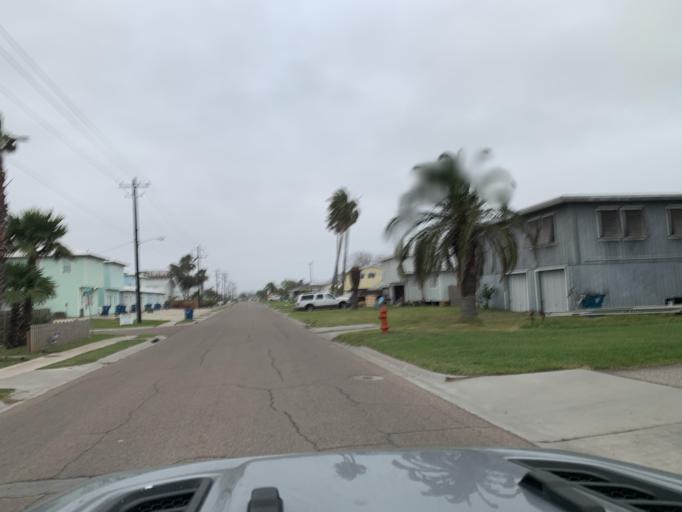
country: US
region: Texas
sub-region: Nueces County
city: Port Aransas
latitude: 27.8284
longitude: -97.0629
